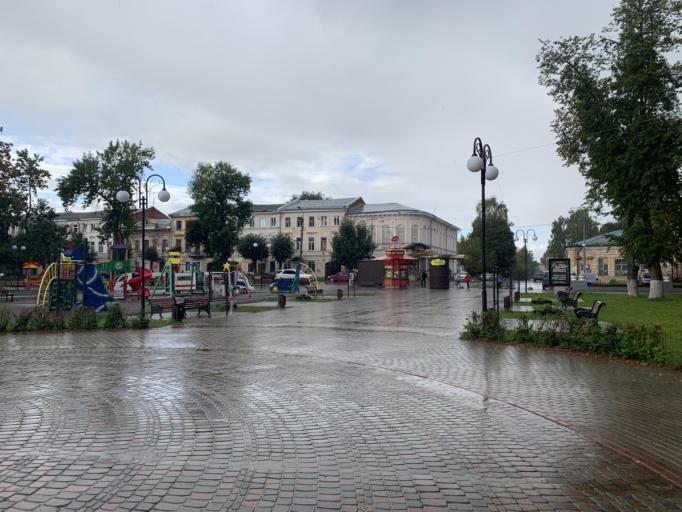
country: RU
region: Tverskaya
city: Vyshniy Volochek
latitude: 57.5842
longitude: 34.5575
